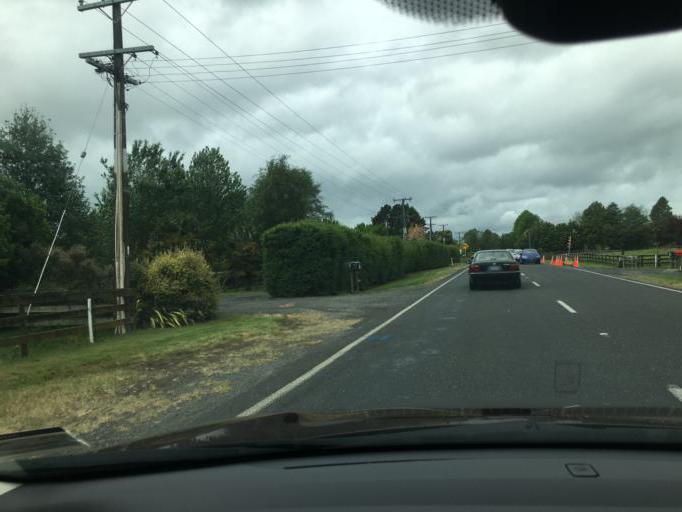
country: NZ
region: Waikato
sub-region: Waipa District
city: Cambridge
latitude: -37.9161
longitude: 175.4451
